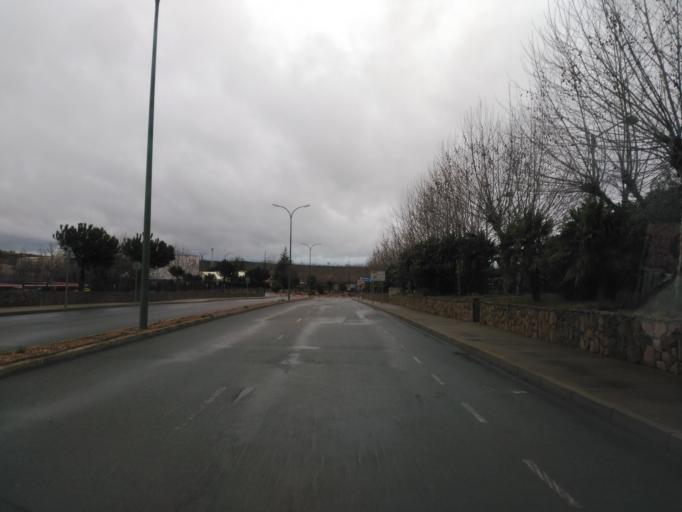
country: ES
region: Castille and Leon
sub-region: Provincia de Salamanca
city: Villamayor
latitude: 40.9829
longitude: -5.7119
